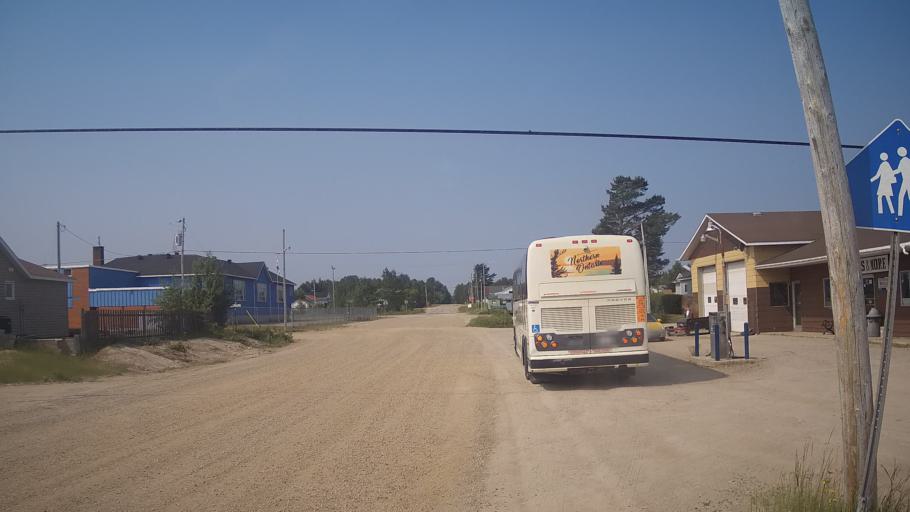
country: CA
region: Ontario
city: Timmins
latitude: 47.6755
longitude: -81.7244
